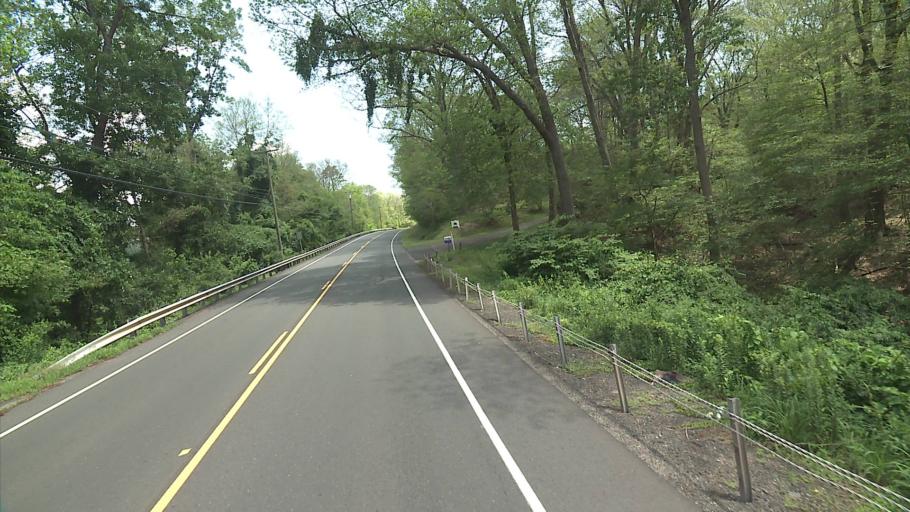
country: US
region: Connecticut
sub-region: Middlesex County
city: Higganum
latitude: 41.4959
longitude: -72.5355
